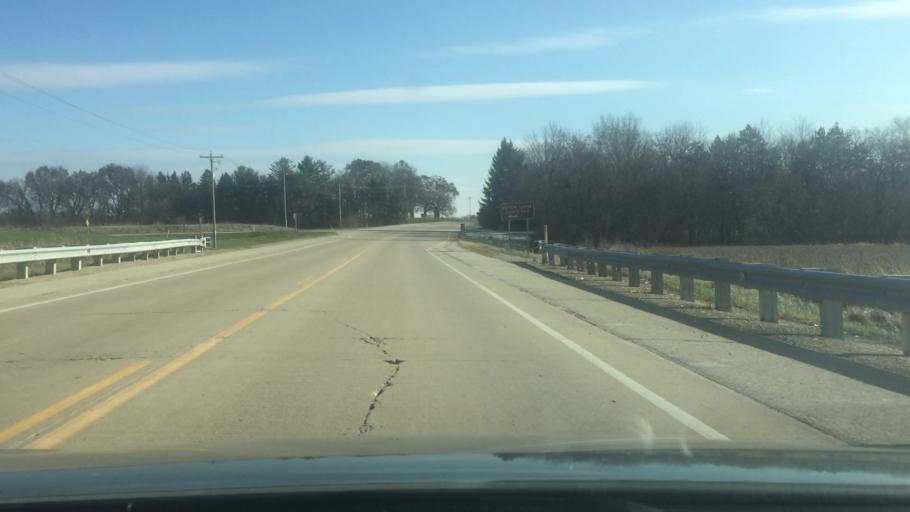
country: US
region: Wisconsin
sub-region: Jefferson County
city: Fort Atkinson
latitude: 42.9561
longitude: -88.8859
